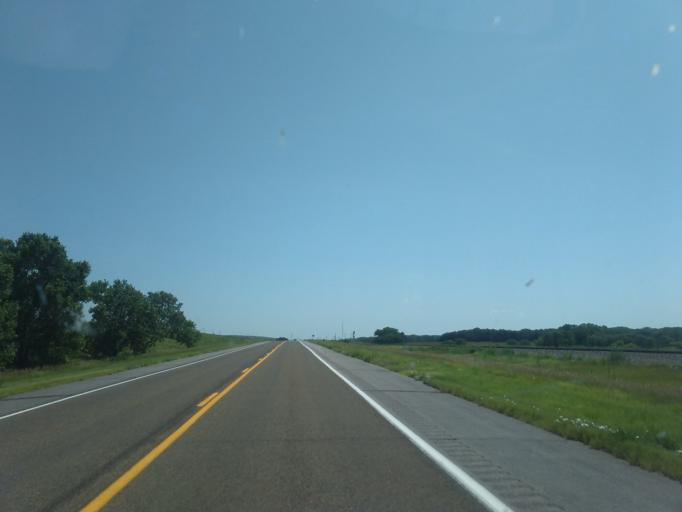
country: US
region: Nebraska
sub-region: Hitchcock County
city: Trenton
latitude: 40.1597
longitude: -101.1672
